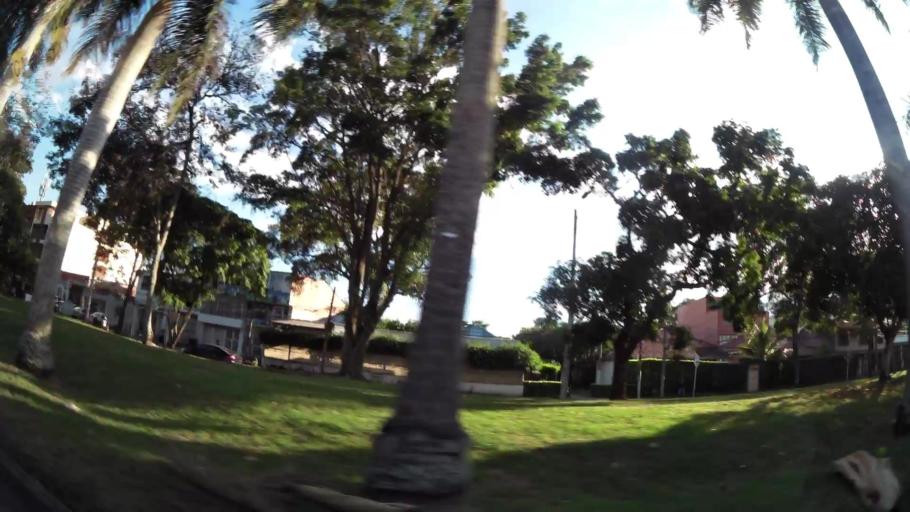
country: CO
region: Valle del Cauca
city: Cali
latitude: 3.4881
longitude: -76.5211
